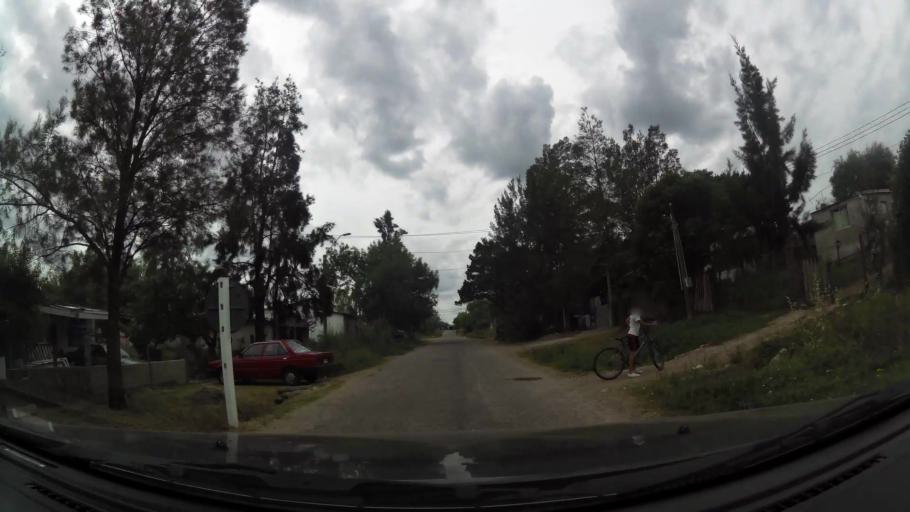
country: UY
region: Canelones
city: Las Piedras
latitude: -34.7123
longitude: -56.2044
